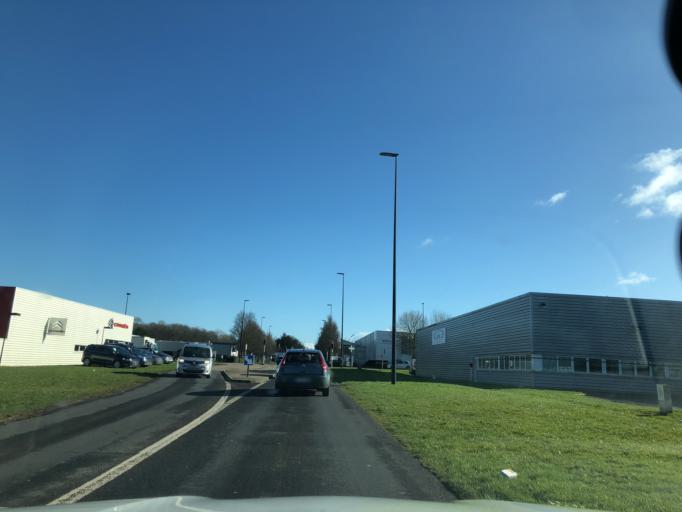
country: FR
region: Lower Normandy
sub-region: Departement du Calvados
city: Epron
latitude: 49.2140
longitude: -0.3453
